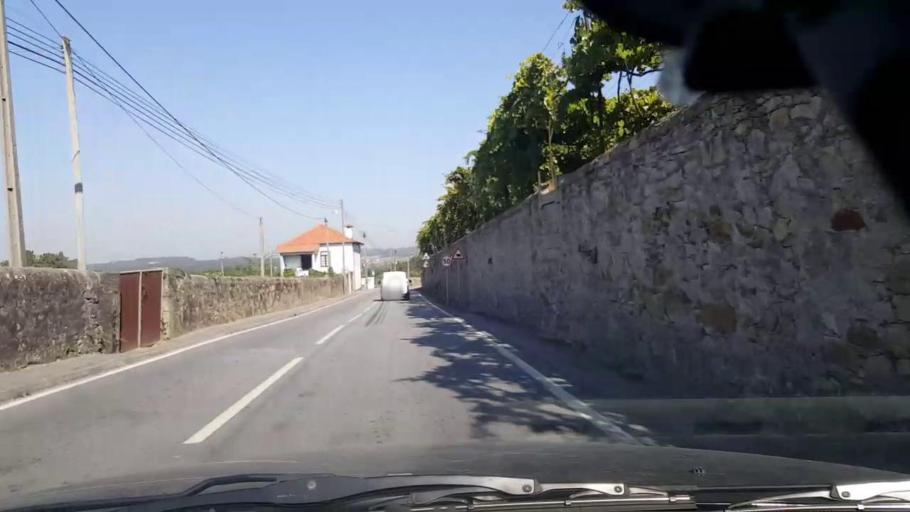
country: PT
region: Porto
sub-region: Vila do Conde
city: Arvore
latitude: 41.3732
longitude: -8.6698
